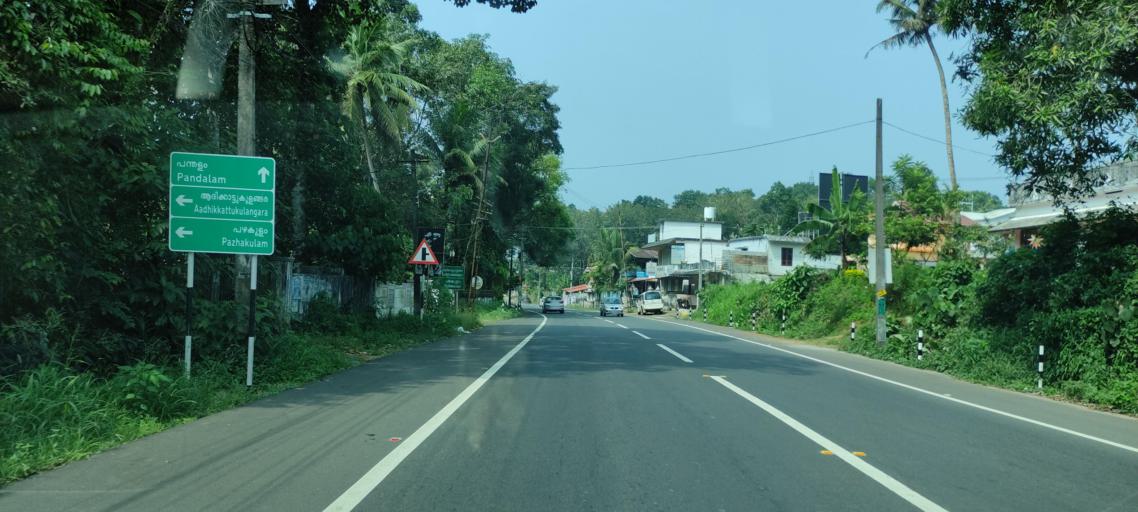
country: IN
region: Kerala
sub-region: Pattanamtitta
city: Adur
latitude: 9.1949
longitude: 76.6998
